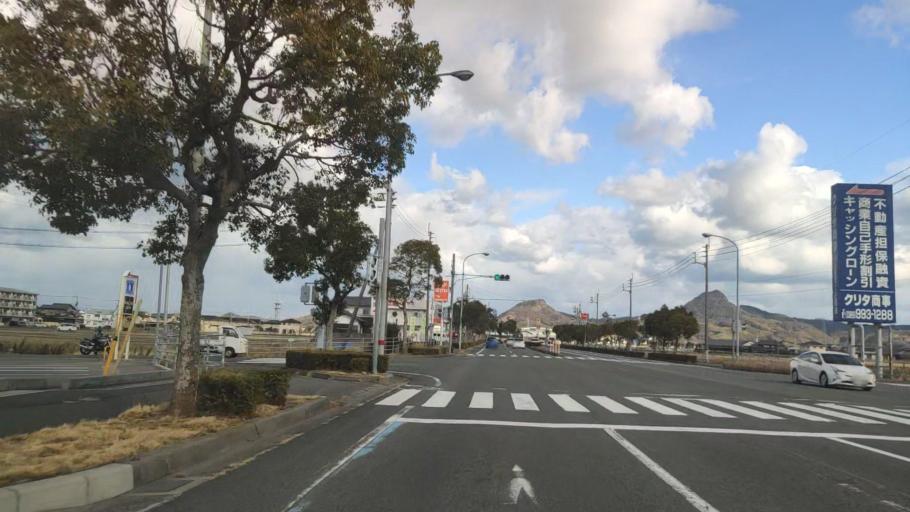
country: JP
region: Ehime
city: Hojo
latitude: 33.9643
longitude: 132.7785
